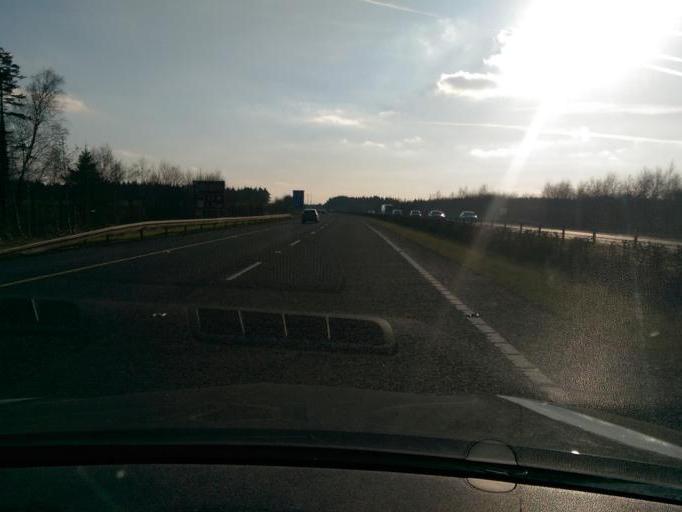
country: IE
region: Leinster
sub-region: Laois
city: Portarlington
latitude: 53.0973
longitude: -7.1595
